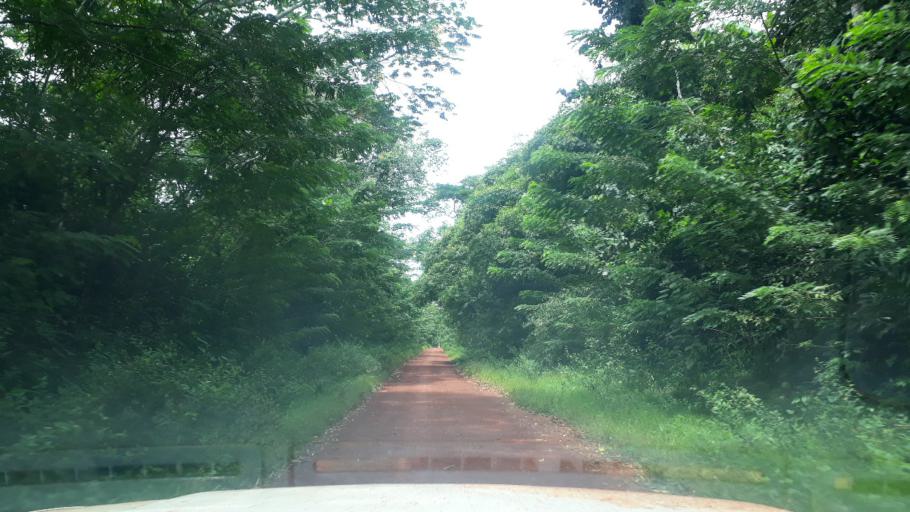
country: CD
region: Eastern Province
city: Aketi
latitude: 2.9304
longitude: 24.0898
